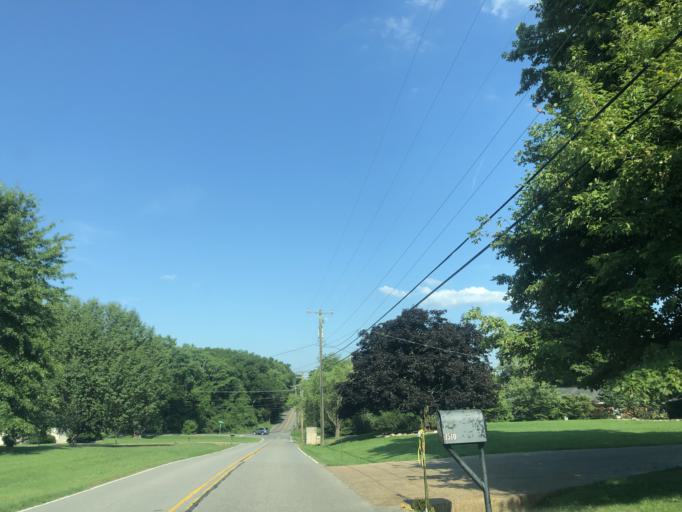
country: US
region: Tennessee
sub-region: Wilson County
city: Green Hill
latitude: 36.1439
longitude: -86.5871
